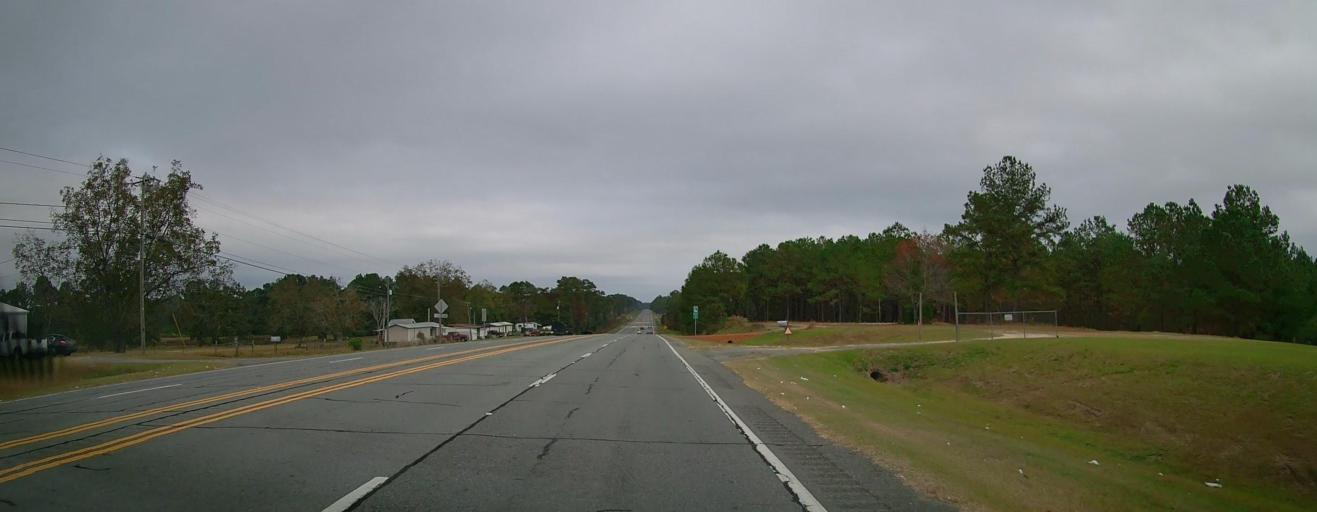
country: US
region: Georgia
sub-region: Tift County
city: Omega
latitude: 31.2949
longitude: -83.6634
